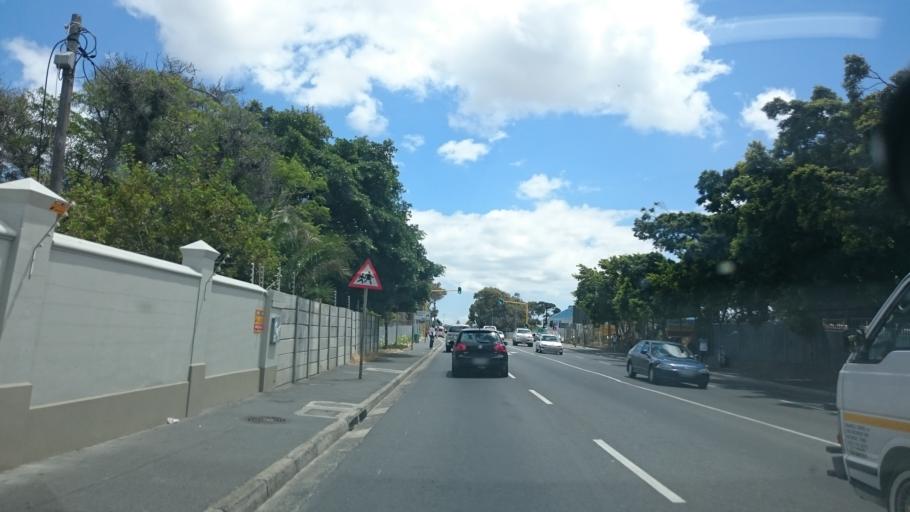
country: ZA
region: Western Cape
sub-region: City of Cape Town
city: Bergvliet
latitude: -34.0611
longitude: 18.4598
